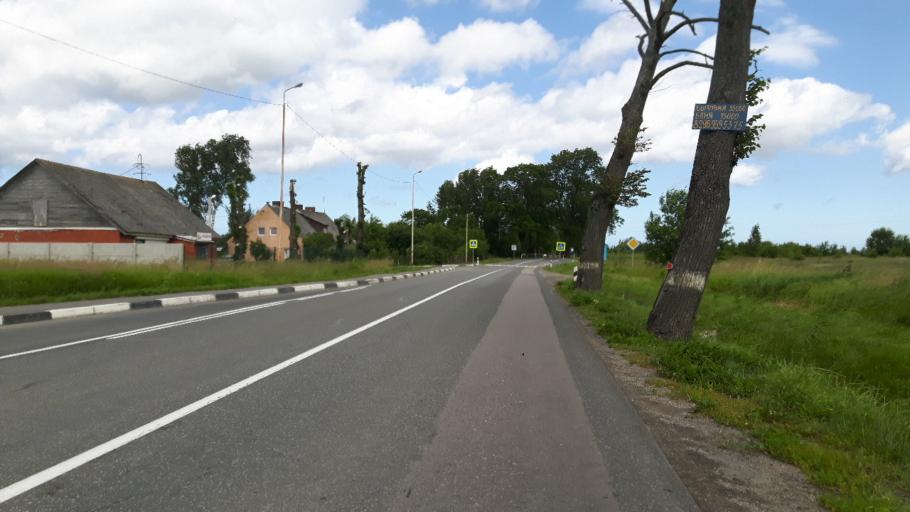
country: RU
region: Kaliningrad
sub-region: Zelenogradskiy Rayon
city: Zelenogradsk
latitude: 54.8908
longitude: 20.4011
